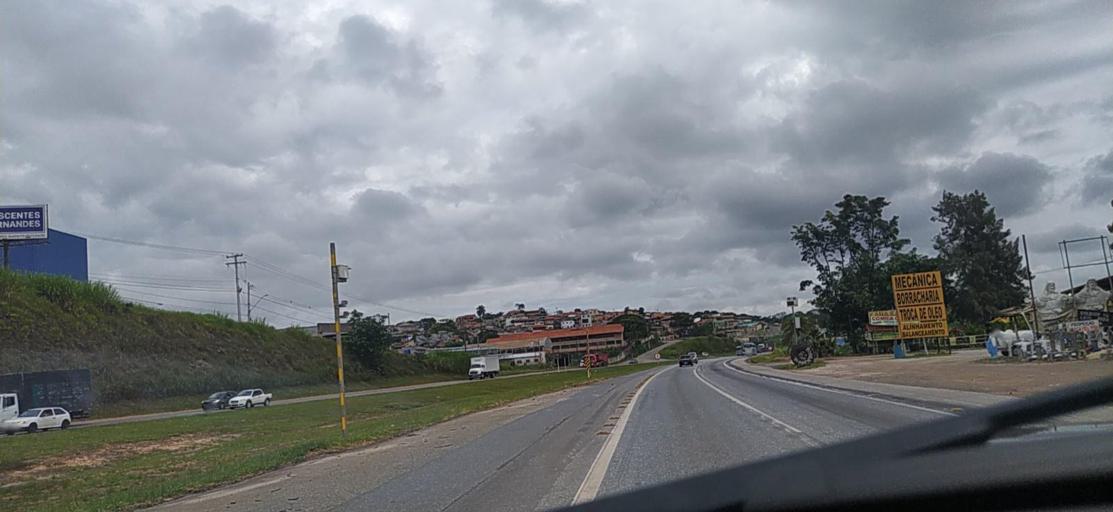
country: BR
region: Minas Gerais
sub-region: Ribeirao Das Neves
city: Ribeirao das Neves
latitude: -19.8319
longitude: -44.0823
